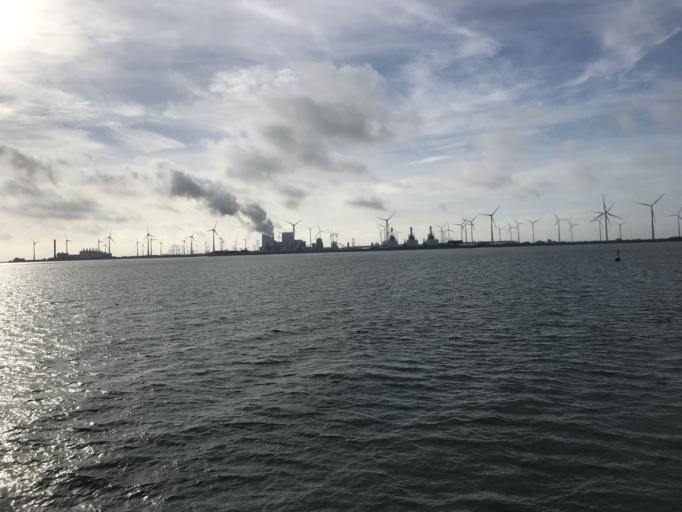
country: NL
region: Groningen
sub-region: Gemeente Appingedam
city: Appingedam
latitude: 53.4685
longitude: 6.8641
